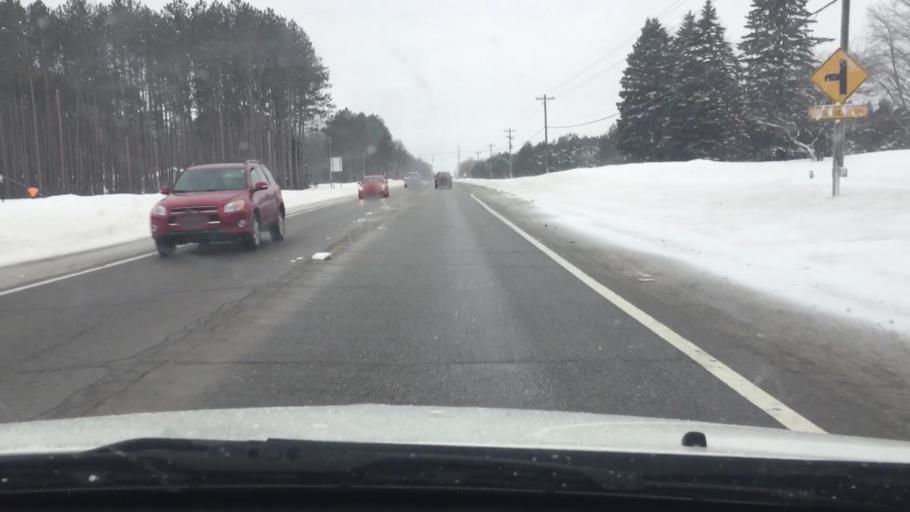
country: US
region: Michigan
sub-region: Otsego County
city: Gaylord
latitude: 45.0277
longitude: -84.7437
